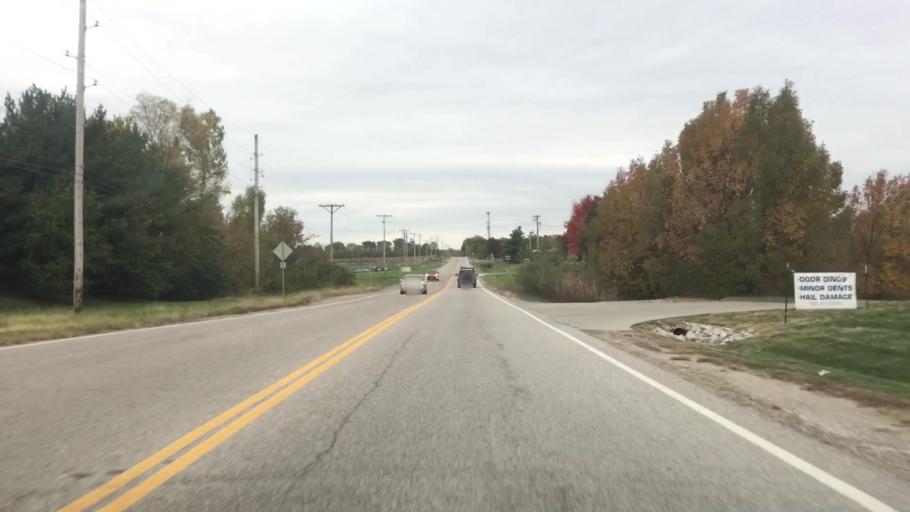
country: US
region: Missouri
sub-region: Jackson County
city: Lees Summit
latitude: 38.8952
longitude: -94.3589
